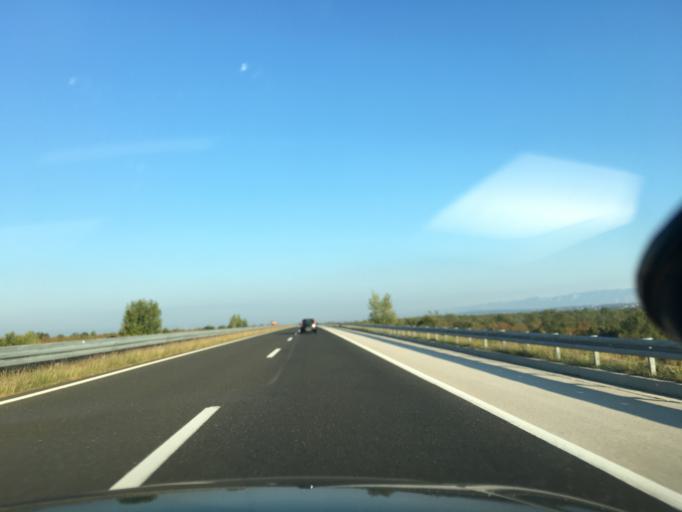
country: HR
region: Zadarska
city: Benkovac
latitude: 43.9752
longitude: 15.6431
